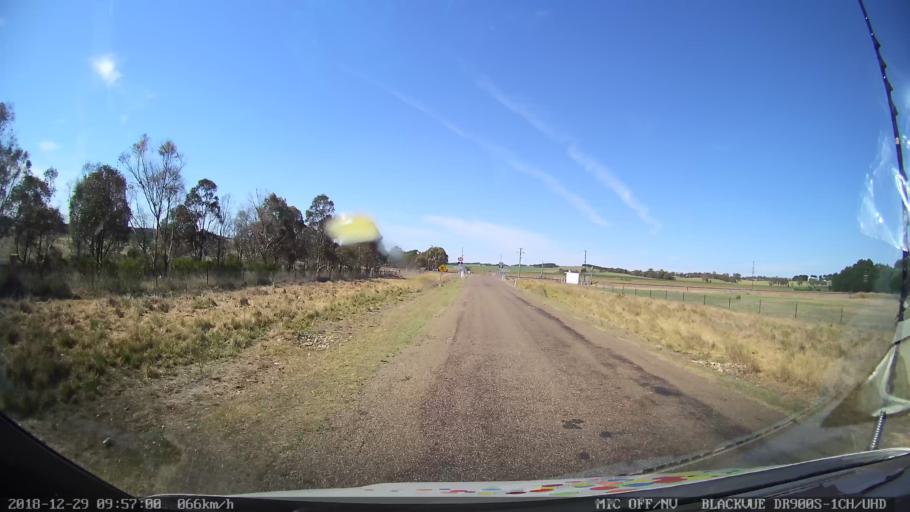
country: AU
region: New South Wales
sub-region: Goulburn Mulwaree
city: Goulburn
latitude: -34.7826
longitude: 149.4812
